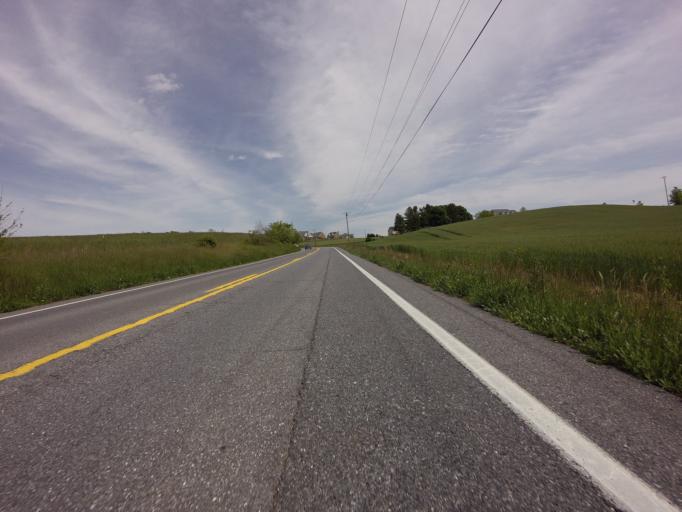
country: US
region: Maryland
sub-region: Frederick County
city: Linganore
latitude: 39.4945
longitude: -77.1821
